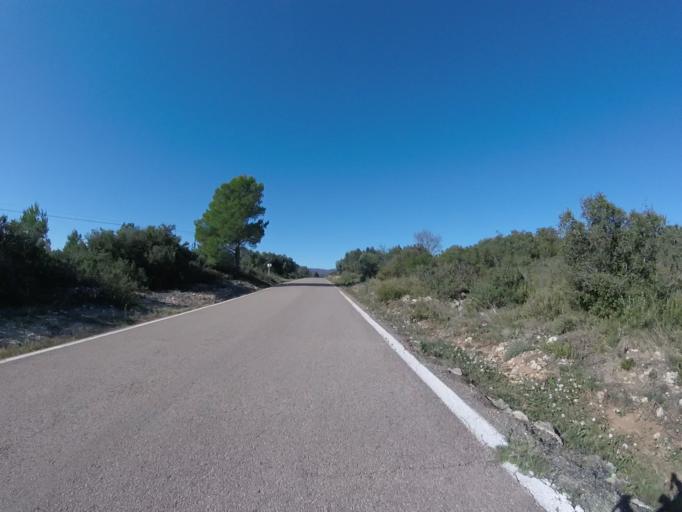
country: ES
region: Valencia
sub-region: Provincia de Castello
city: Chert/Xert
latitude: 40.4558
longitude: 0.1389
